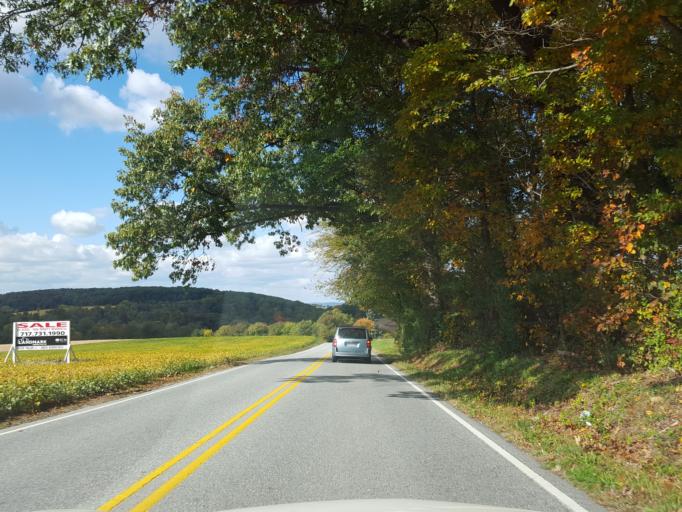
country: US
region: Pennsylvania
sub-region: York County
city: Yoe
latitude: 39.9205
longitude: -76.6367
